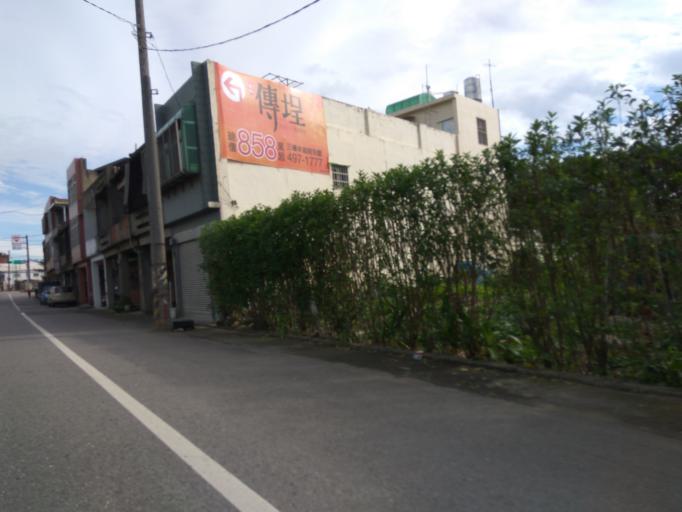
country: TW
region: Taiwan
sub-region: Hsinchu
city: Zhubei
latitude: 24.9658
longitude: 121.0979
